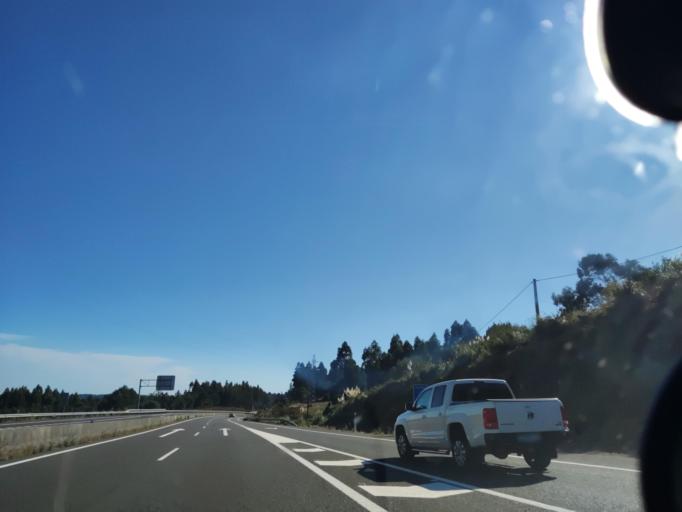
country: ES
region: Galicia
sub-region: Provincia da Coruna
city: Boiro
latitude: 42.5849
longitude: -8.9850
